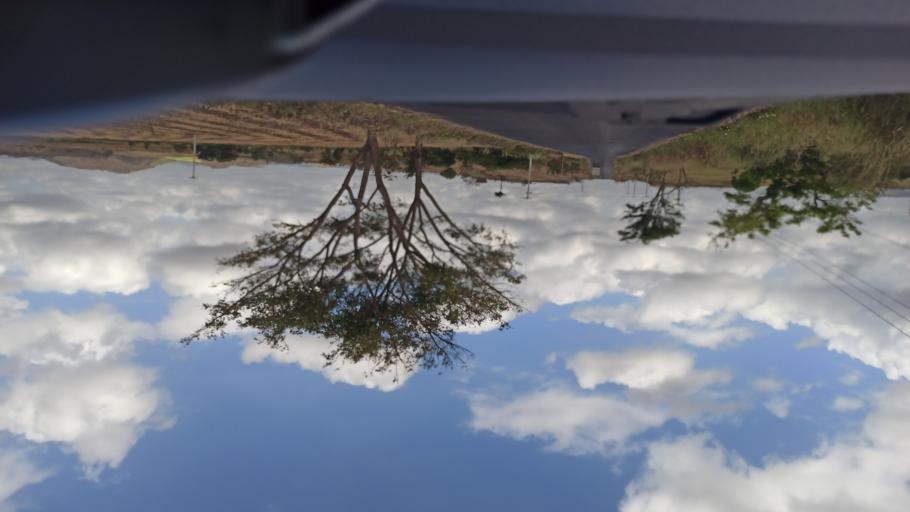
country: BR
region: Pernambuco
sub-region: Timbauba
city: Timbauba
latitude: -7.4763
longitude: -35.2811
